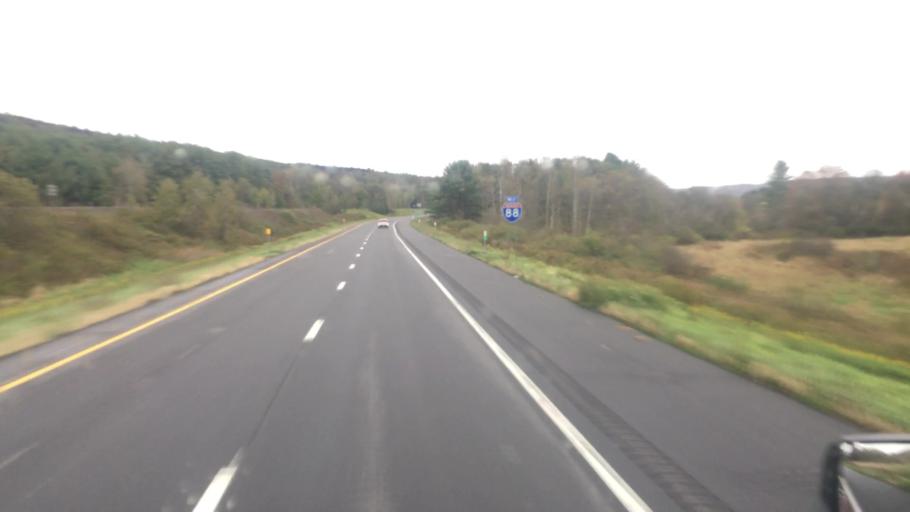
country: US
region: New York
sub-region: Chenango County
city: Bainbridge
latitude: 42.2174
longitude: -75.5146
